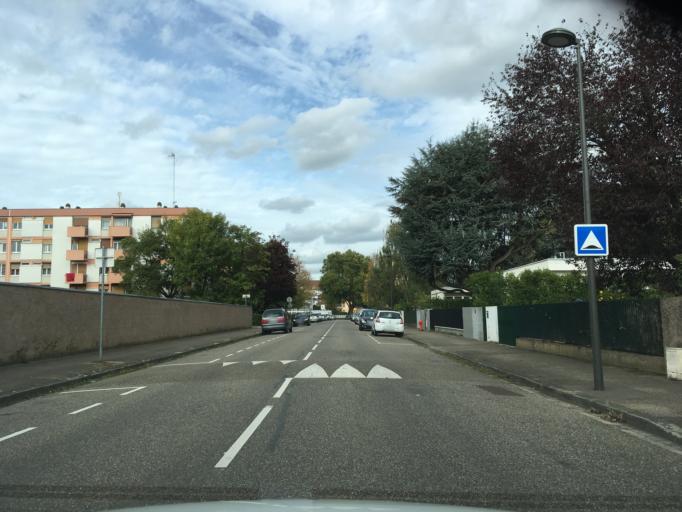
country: FR
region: Alsace
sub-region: Departement du Bas-Rhin
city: Strasbourg
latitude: 48.5635
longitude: 7.7756
